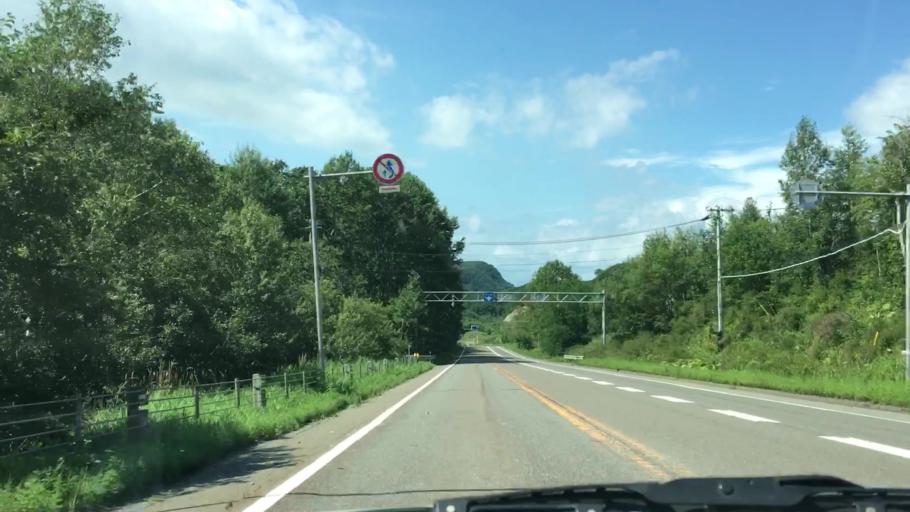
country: JP
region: Hokkaido
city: Otofuke
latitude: 43.2333
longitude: 143.4950
